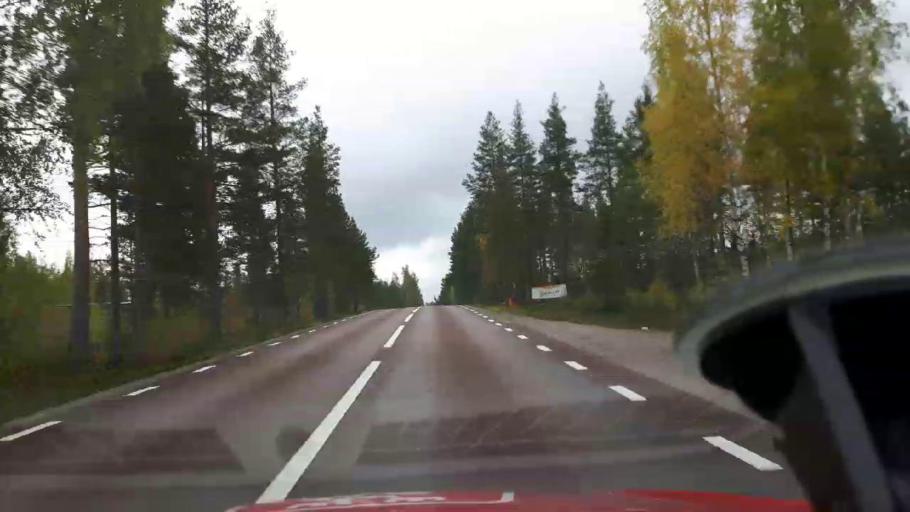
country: SE
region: Jaemtland
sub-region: Harjedalens Kommun
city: Sveg
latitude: 62.2056
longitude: 14.8483
